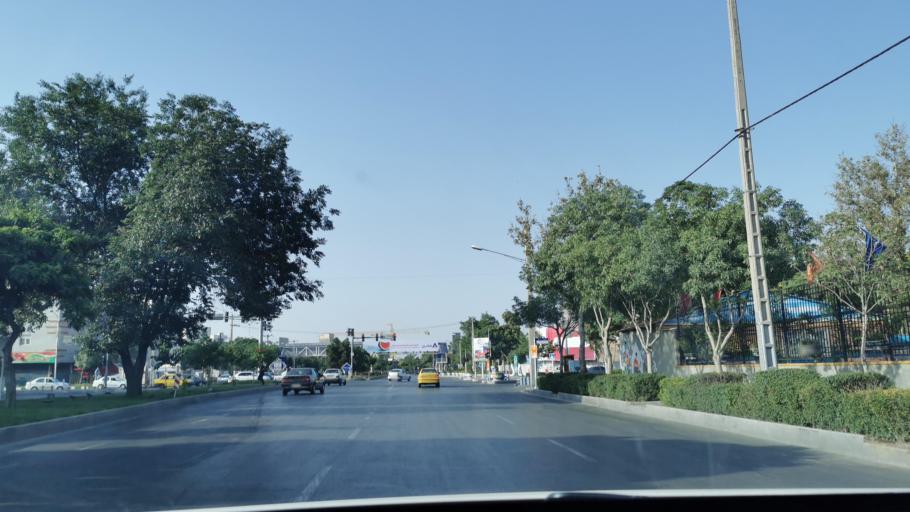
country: IR
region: Razavi Khorasan
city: Mashhad
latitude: 36.2900
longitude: 59.6305
